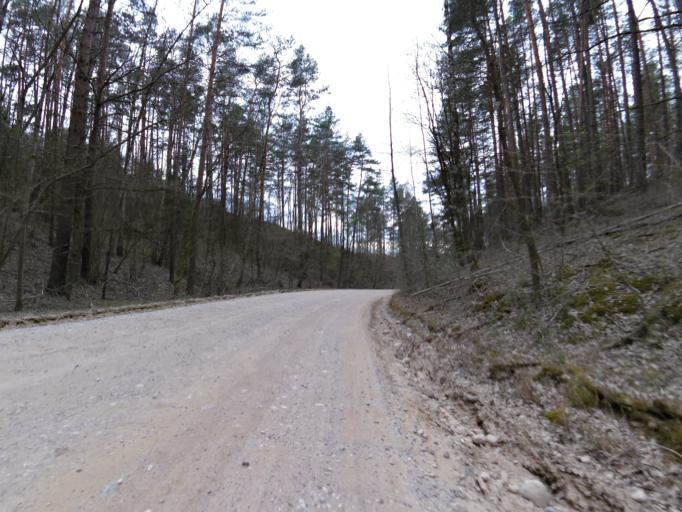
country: LT
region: Vilnius County
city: Pilaite
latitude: 54.6777
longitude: 25.1800
